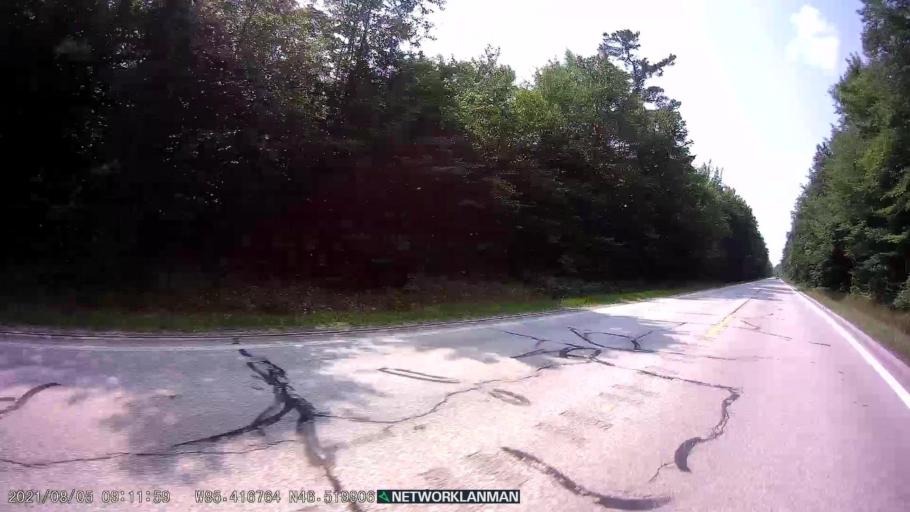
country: US
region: Michigan
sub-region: Luce County
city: Newberry
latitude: 46.5196
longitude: -85.4172
